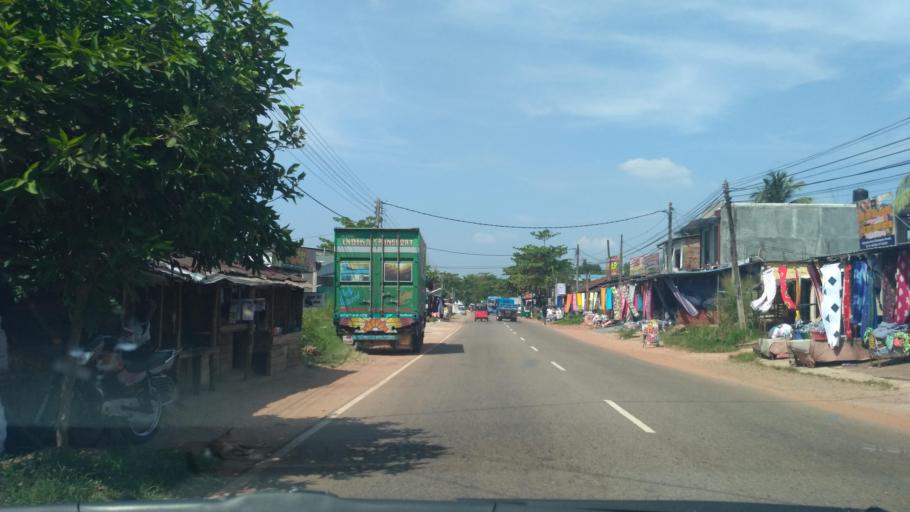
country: LK
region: North Western
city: Kuliyapitiya
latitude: 7.3493
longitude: 80.0314
